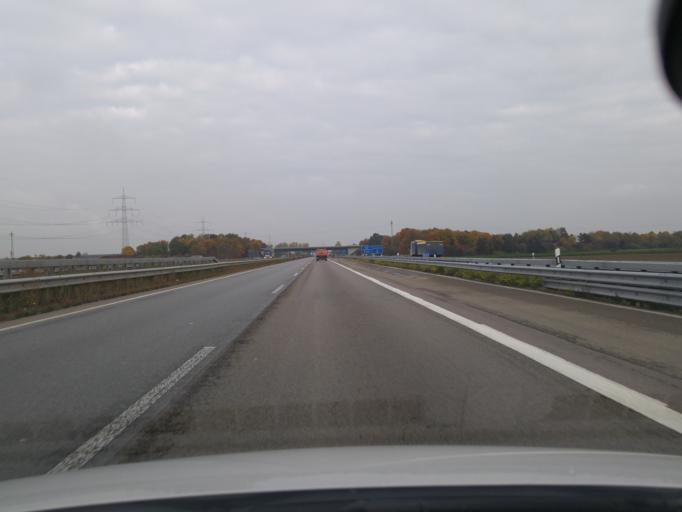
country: DE
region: Rheinland-Pfalz
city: Dannstadt-Schauernheim
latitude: 49.4387
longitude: 8.3271
